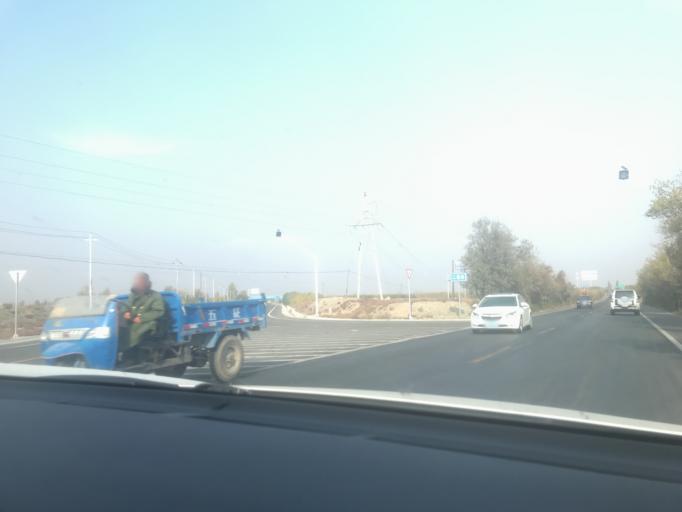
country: CN
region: Gansu Sheng
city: Gulang
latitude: 37.6305
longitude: 103.0913
